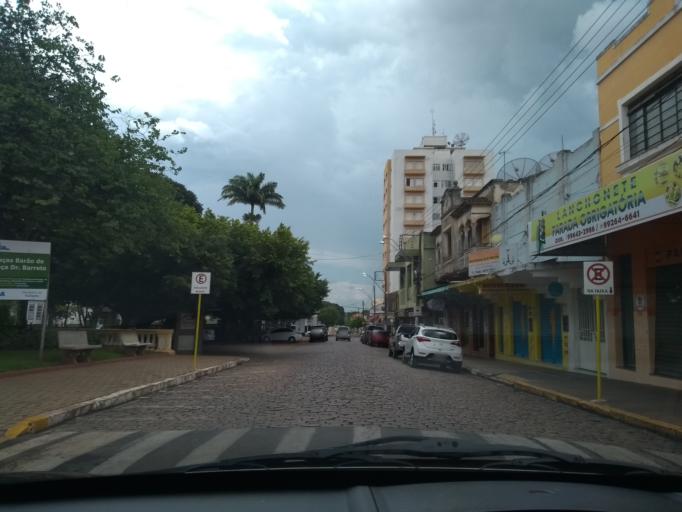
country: BR
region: Sao Paulo
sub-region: Casa Branca
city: Casa Branca
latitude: -21.7734
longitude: -47.0850
